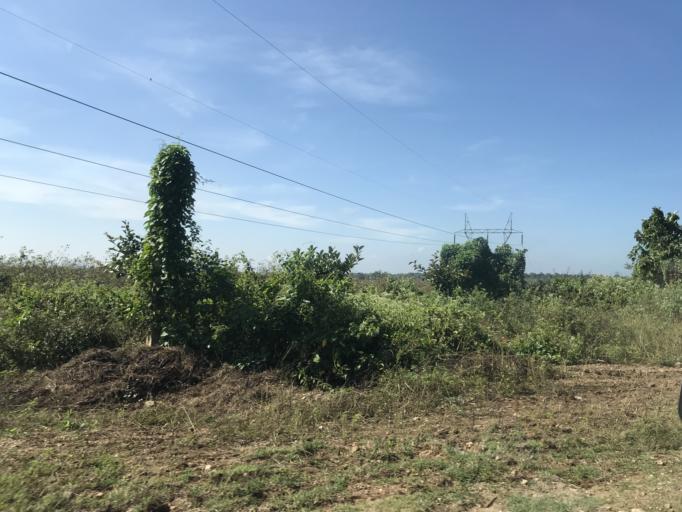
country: IN
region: Karnataka
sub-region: Mysore
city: Heggadadevankote
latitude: 12.0158
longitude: 76.2667
